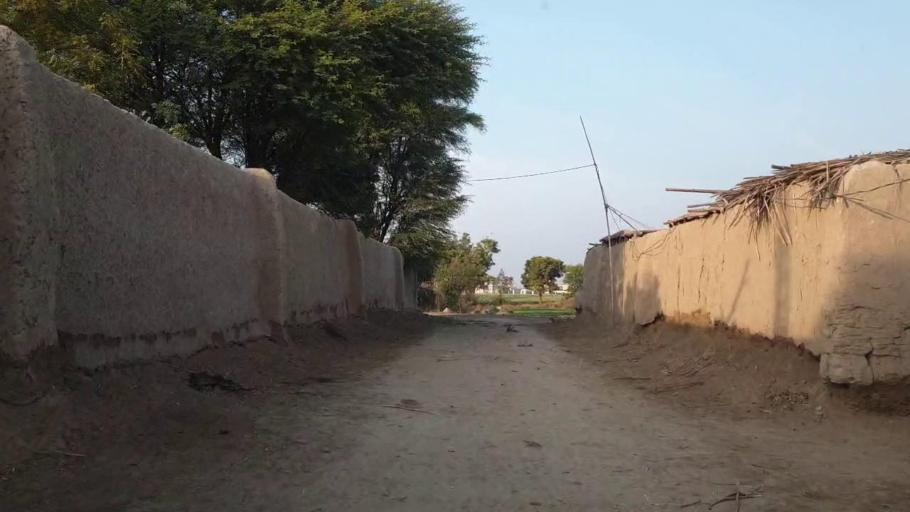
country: PK
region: Sindh
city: Matiari
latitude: 25.6000
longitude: 68.4370
